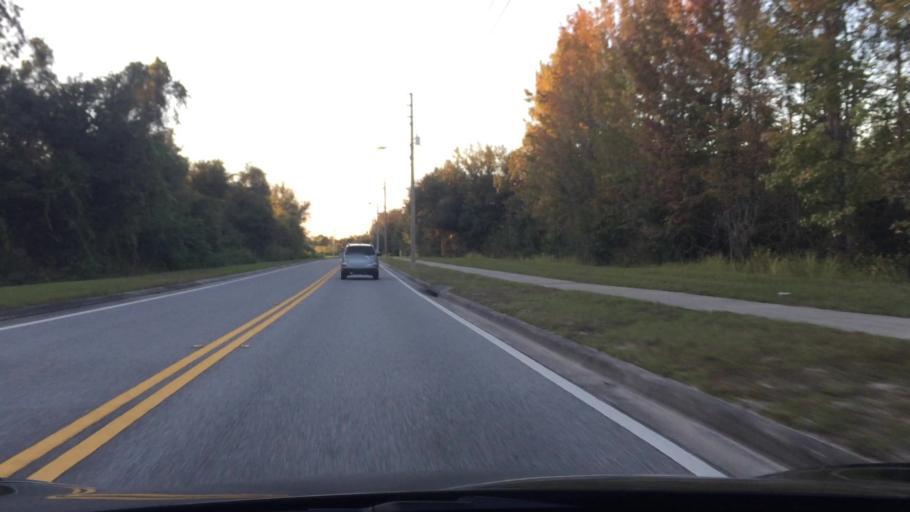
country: US
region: Florida
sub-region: Hillsborough County
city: Lutz
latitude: 28.1741
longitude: -82.4374
